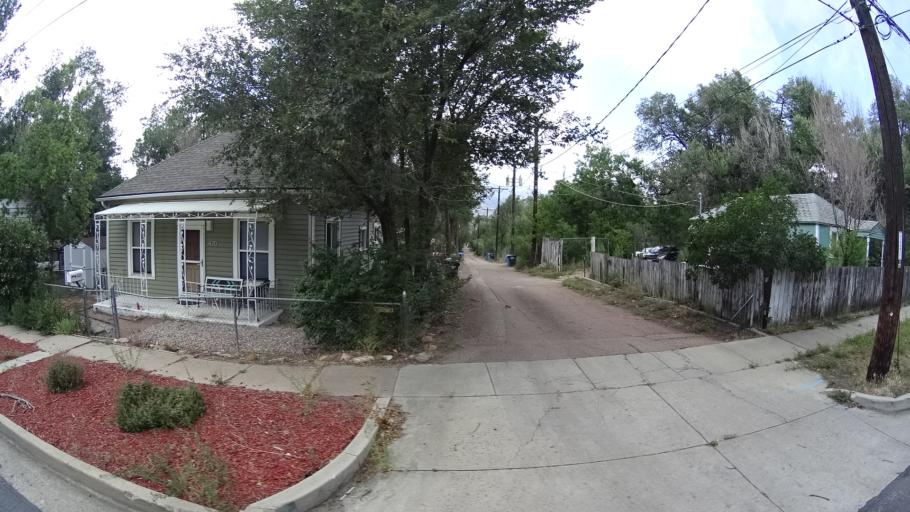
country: US
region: Colorado
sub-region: El Paso County
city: Colorado Springs
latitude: 38.8271
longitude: -104.8083
